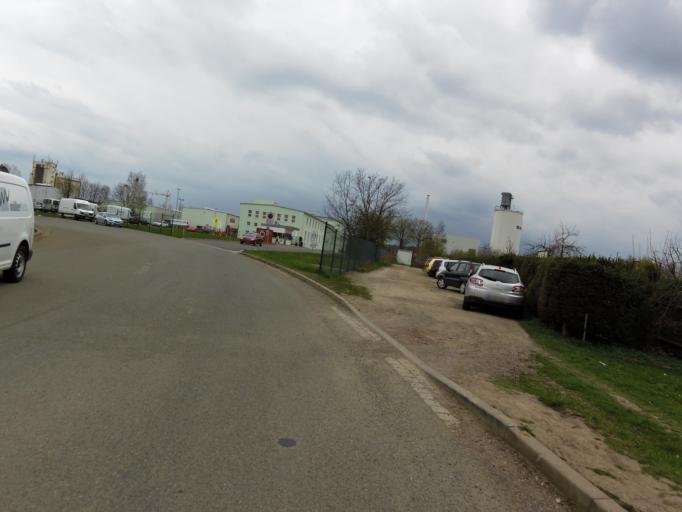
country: DE
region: Thuringia
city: Gotha
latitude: 50.9529
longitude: 10.7202
